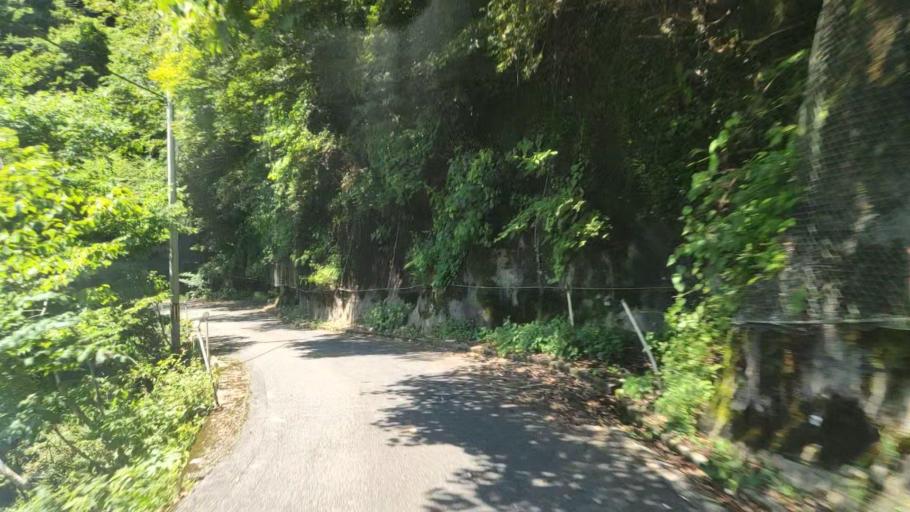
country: JP
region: Gifu
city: Godo
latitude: 35.6944
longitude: 136.5722
